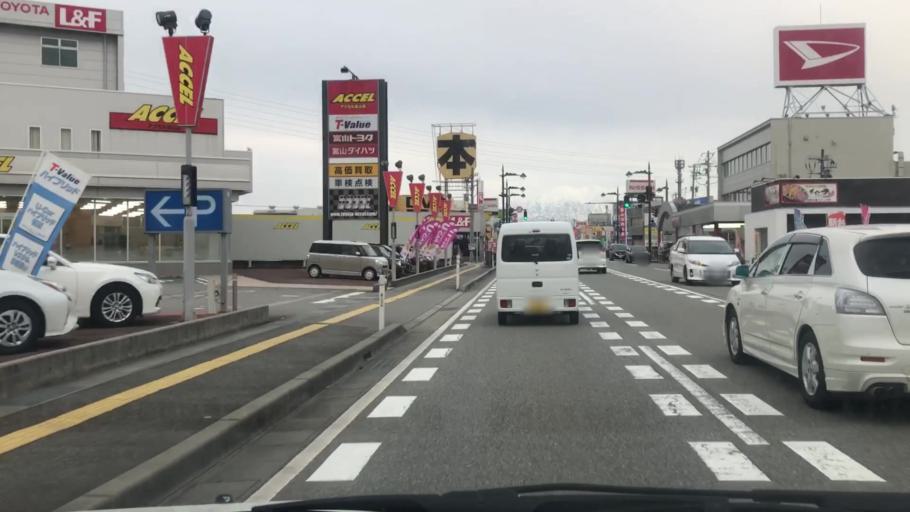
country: JP
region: Toyama
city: Toyama-shi
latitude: 36.6960
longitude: 137.2416
